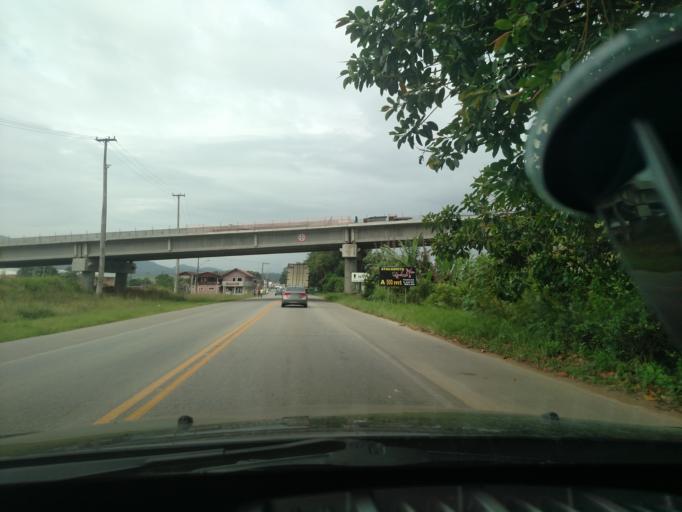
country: BR
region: Santa Catarina
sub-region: Gaspar
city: Gaspar
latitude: -26.8946
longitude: -48.8234
